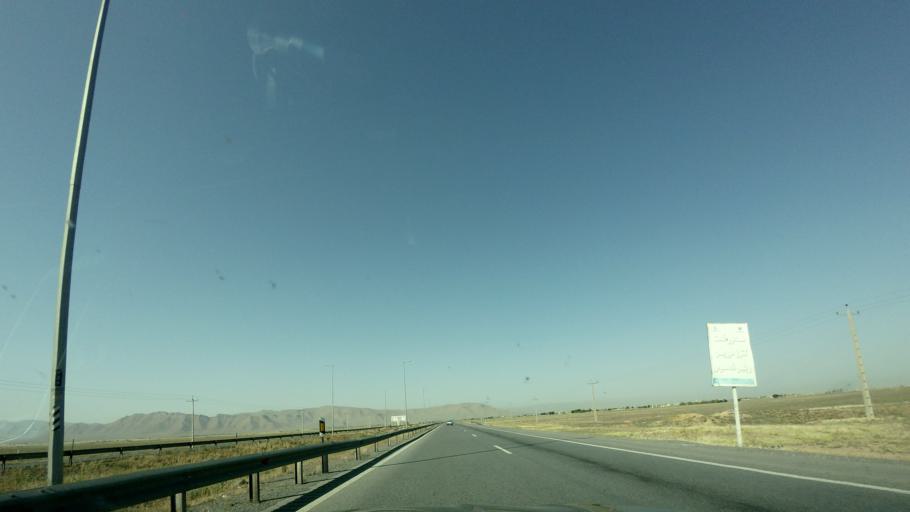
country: IR
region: Markazi
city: Ashtian
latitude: 34.1791
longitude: 50.0435
